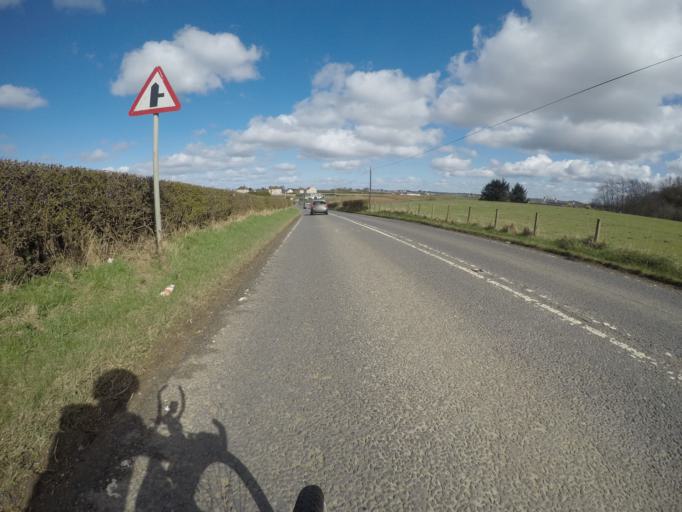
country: GB
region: Scotland
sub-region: East Ayrshire
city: Crosshouse
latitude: 55.5906
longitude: -4.5541
